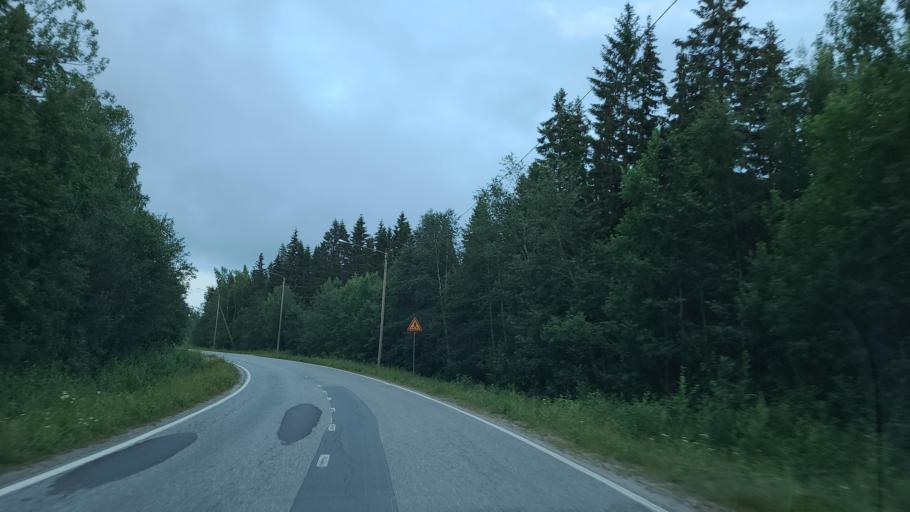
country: FI
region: Ostrobothnia
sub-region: Vaasa
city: Replot
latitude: 63.2861
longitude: 21.1180
